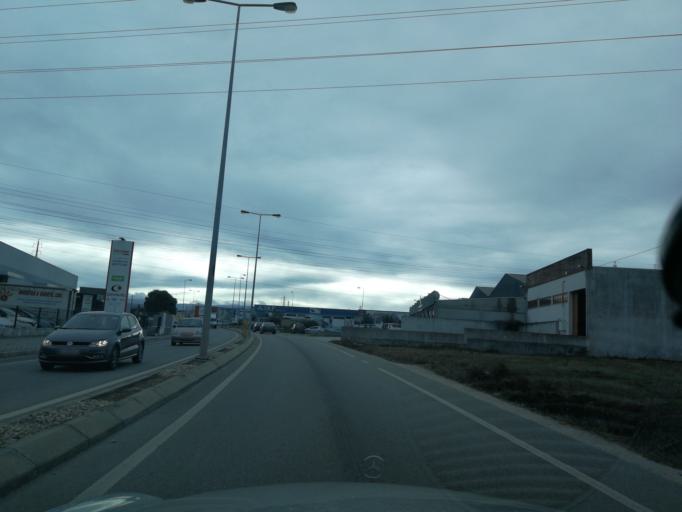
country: PT
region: Aveiro
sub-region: Agueda
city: Agueda
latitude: 40.5945
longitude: -8.4640
